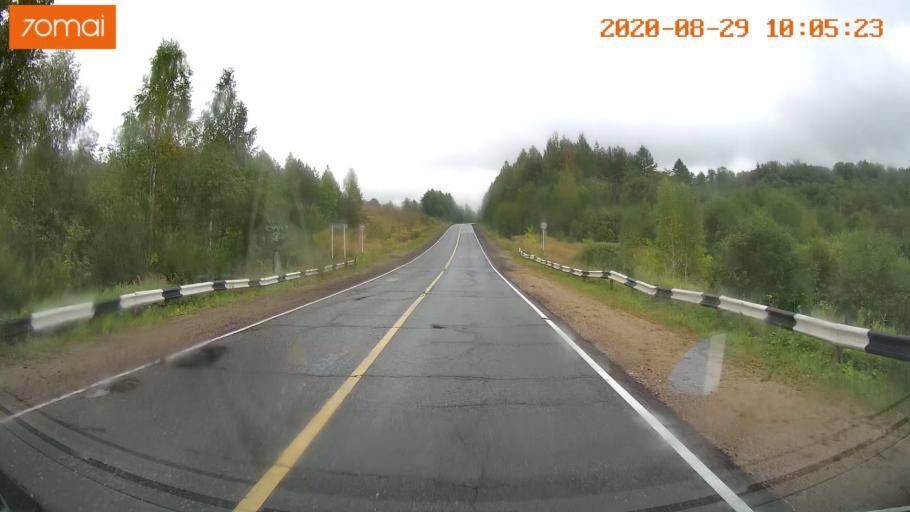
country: RU
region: Ivanovo
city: Zarechnyy
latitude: 57.3930
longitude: 42.5198
